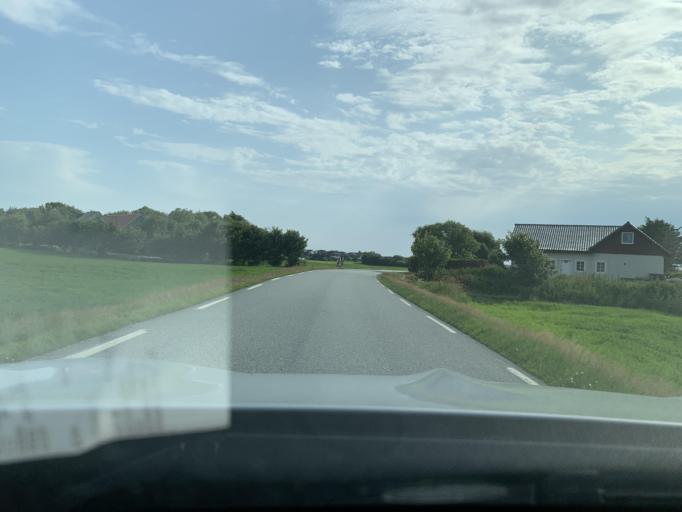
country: NO
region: Rogaland
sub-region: Time
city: Bryne
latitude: 58.7285
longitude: 5.5864
